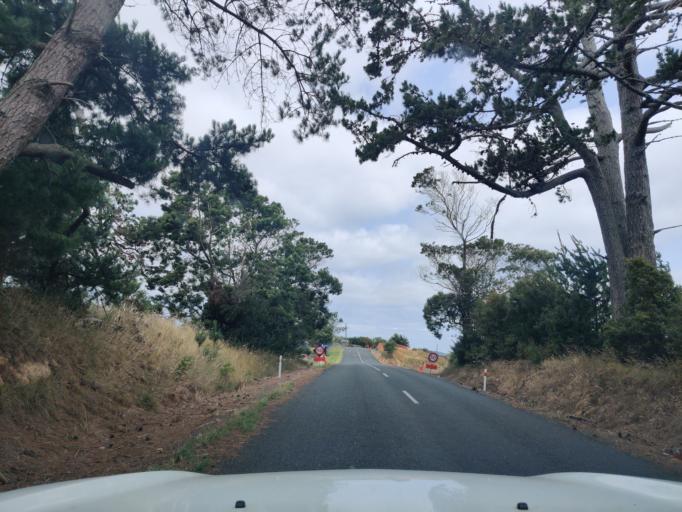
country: NZ
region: Waikato
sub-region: Waikato District
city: Te Kauwhata
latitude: -37.5183
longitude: 175.1770
